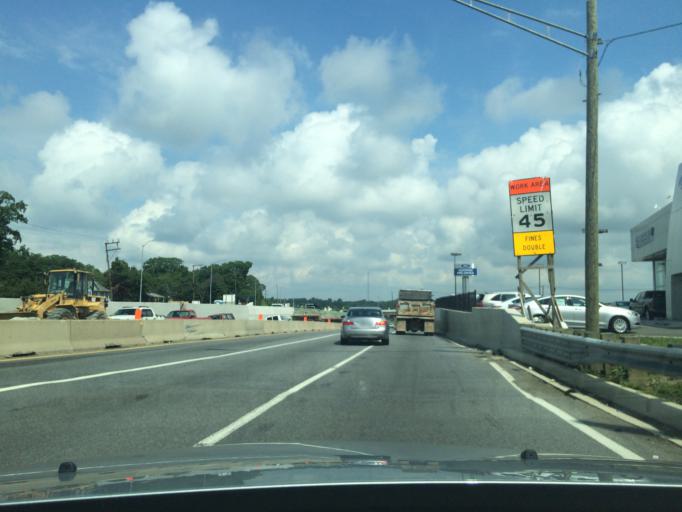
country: US
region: Maryland
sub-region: Prince George's County
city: Camp Springs
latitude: 38.8219
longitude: -76.9210
